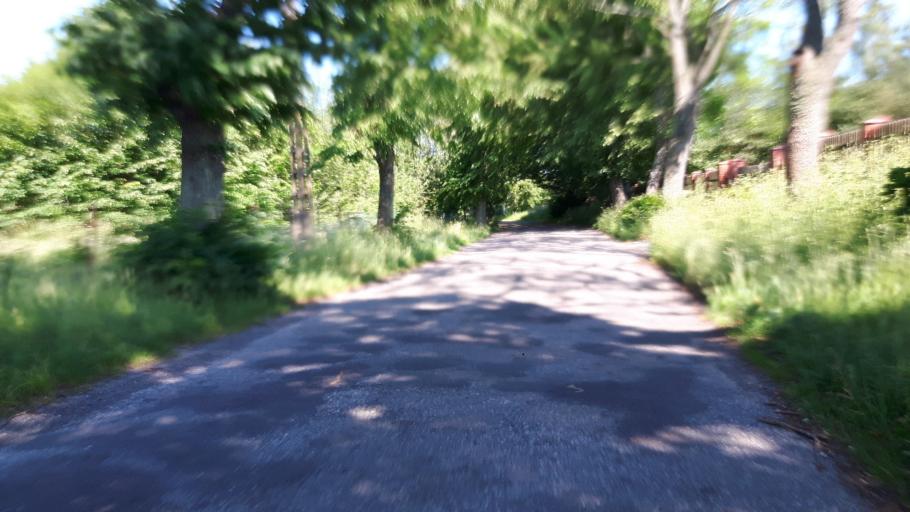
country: PL
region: Pomeranian Voivodeship
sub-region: Powiat slupski
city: Glowczyce
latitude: 54.6783
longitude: 17.4275
